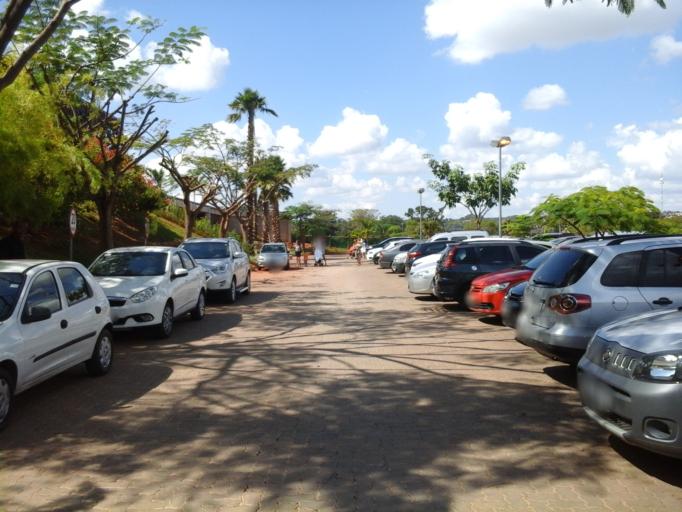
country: BR
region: Federal District
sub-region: Brasilia
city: Brasilia
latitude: -15.8181
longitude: -47.8371
